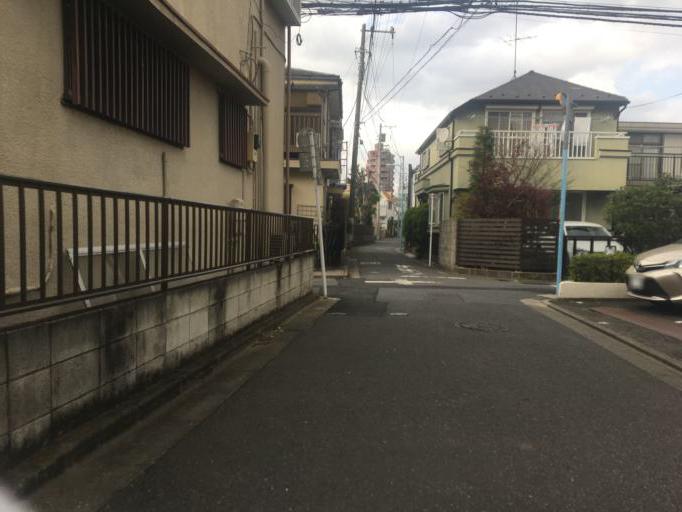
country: JP
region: Tokyo
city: Tokyo
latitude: 35.7001
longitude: 139.6281
